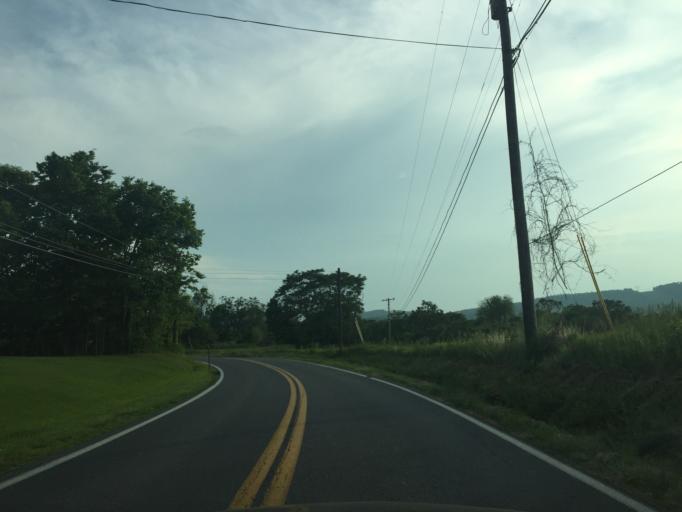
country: US
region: Maryland
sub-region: Frederick County
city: Adamstown
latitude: 39.3030
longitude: -77.5000
